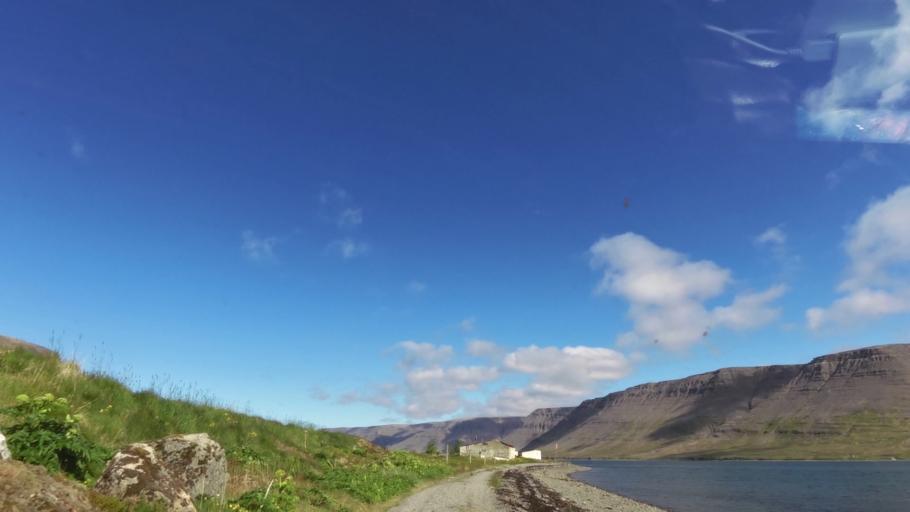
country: IS
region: West
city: Olafsvik
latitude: 65.6200
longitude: -23.8674
